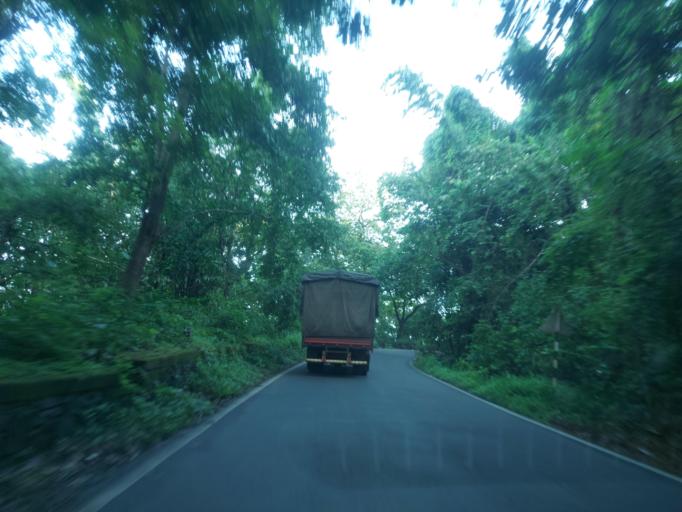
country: IN
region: Maharashtra
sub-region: Sindhudurg
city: Savantvadi
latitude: 15.9355
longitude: 73.9434
